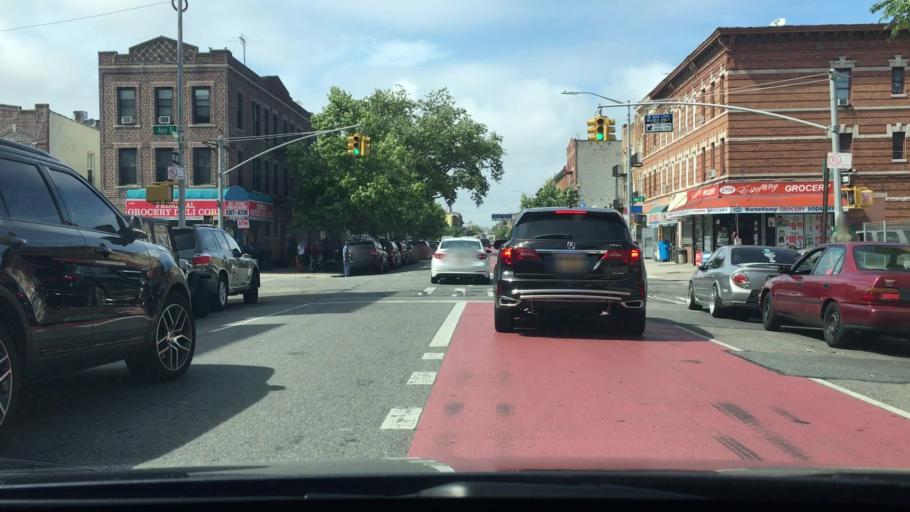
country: US
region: New York
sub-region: Kings County
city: Brooklyn
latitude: 40.6406
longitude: -73.9513
